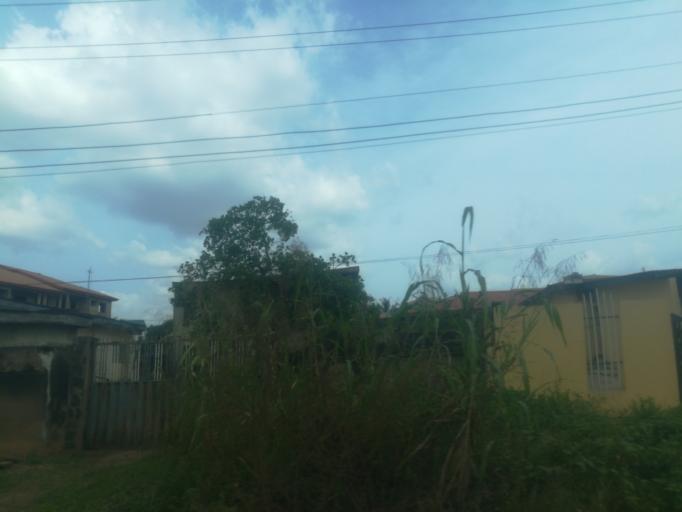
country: NG
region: Ogun
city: Abeokuta
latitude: 7.1267
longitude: 3.3207
